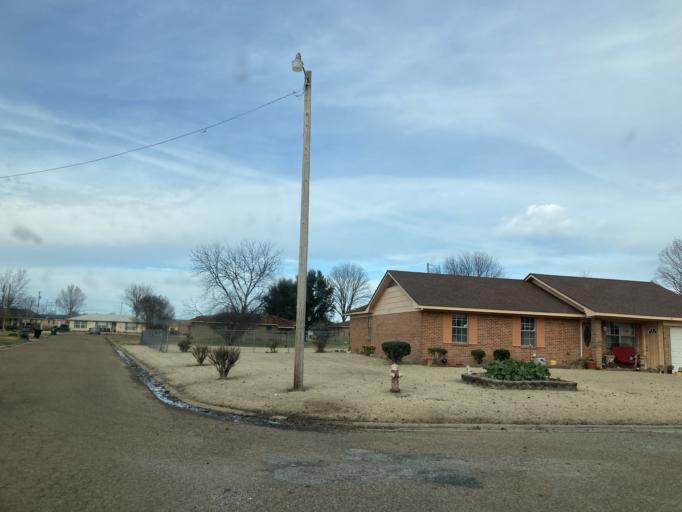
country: US
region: Mississippi
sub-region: Humphreys County
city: Belzoni
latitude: 33.1711
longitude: -90.5037
